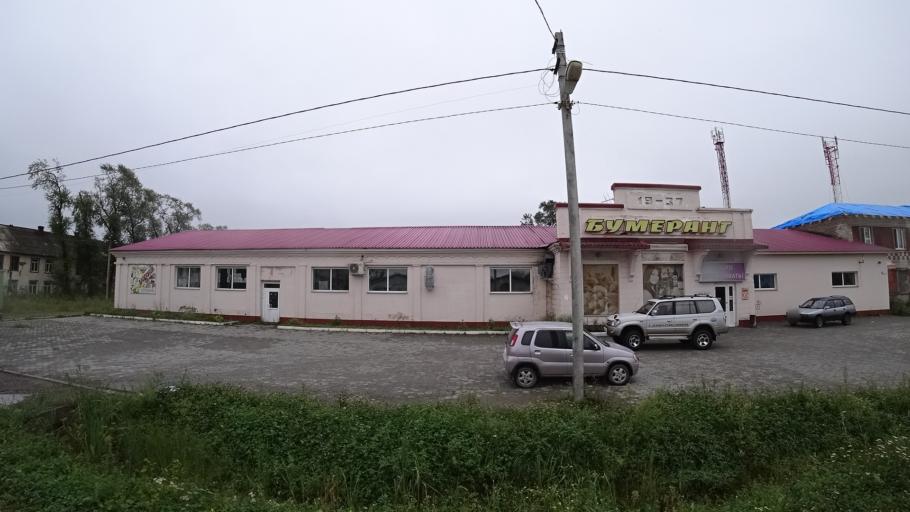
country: RU
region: Primorskiy
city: Monastyrishche
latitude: 44.1963
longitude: 132.4266
